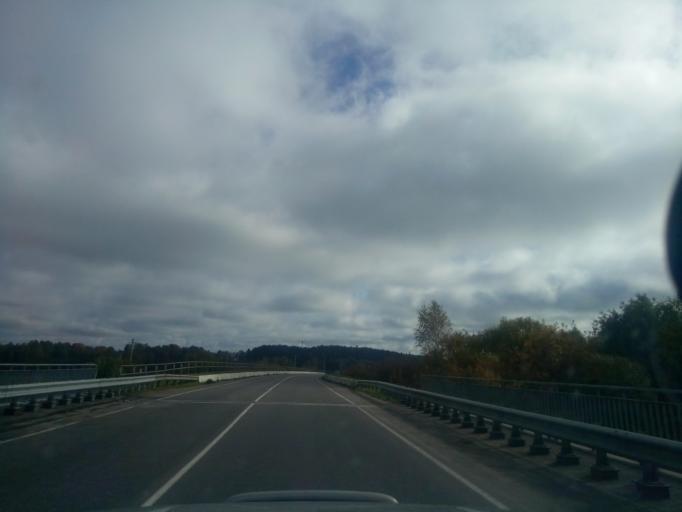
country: BY
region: Minsk
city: Zaslawye
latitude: 53.9994
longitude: 27.2831
